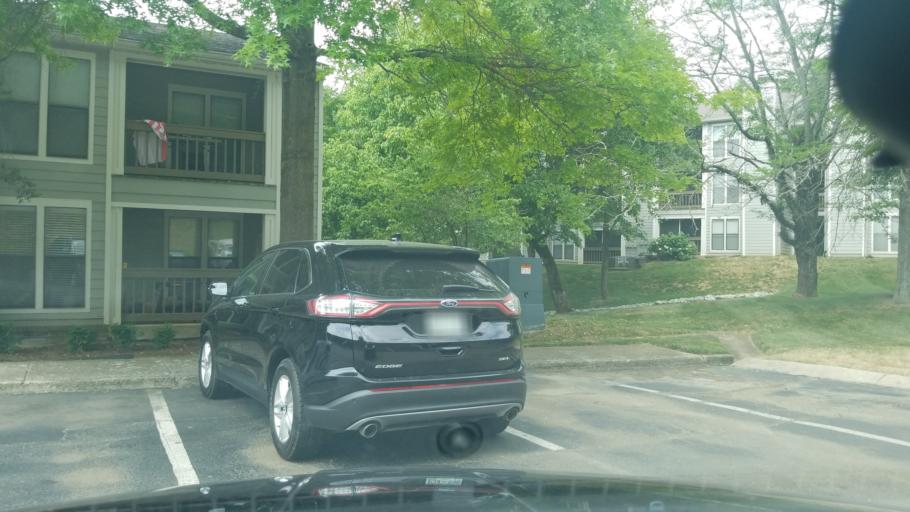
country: US
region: Tennessee
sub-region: Davidson County
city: Goodlettsville
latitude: 36.2680
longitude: -86.7420
